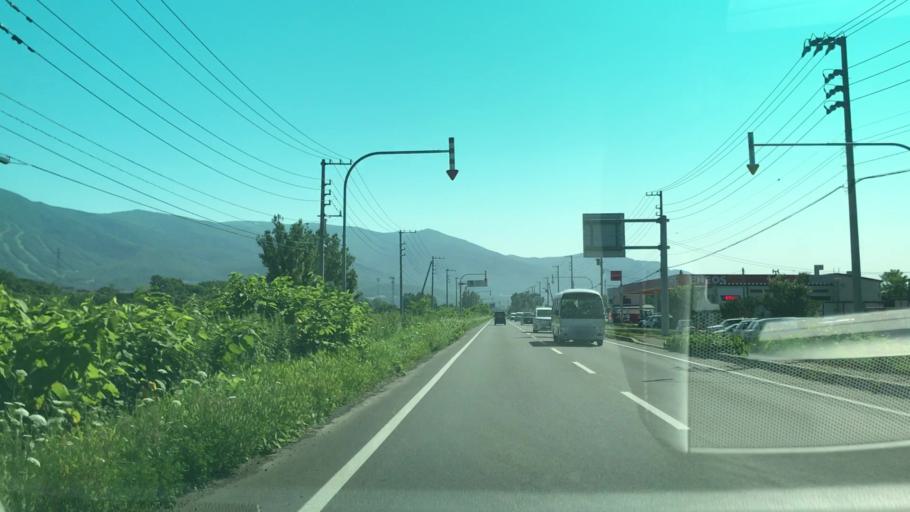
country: JP
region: Hokkaido
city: Iwanai
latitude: 42.9965
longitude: 140.5369
